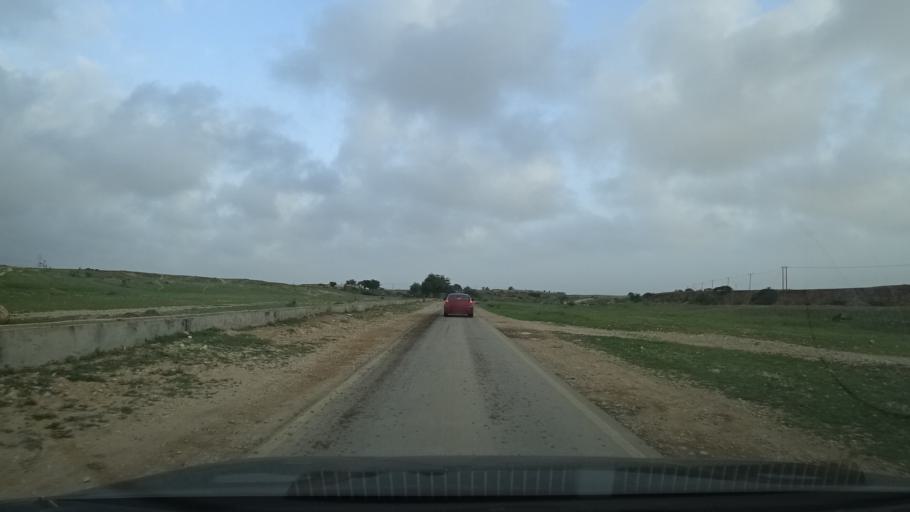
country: OM
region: Zufar
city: Salalah
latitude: 17.1034
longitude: 54.2320
